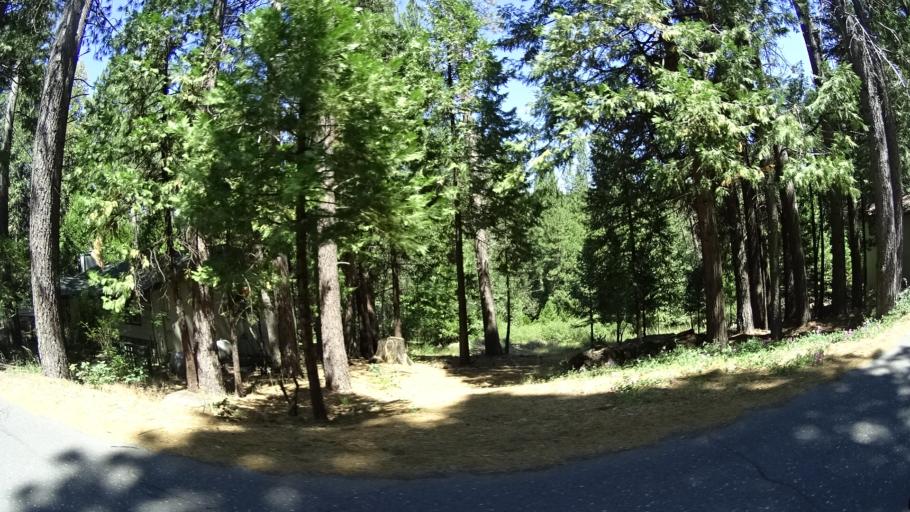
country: US
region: California
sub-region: Calaveras County
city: Arnold
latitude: 38.2343
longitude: -120.3686
